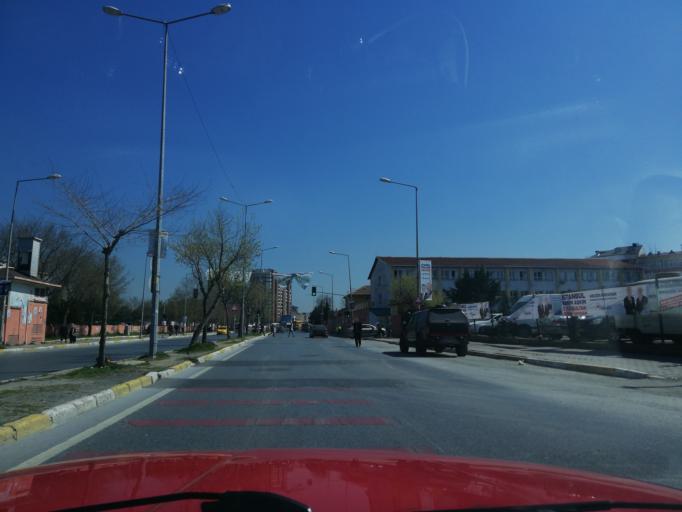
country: TR
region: Istanbul
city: Sisli
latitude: 41.0800
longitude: 28.9329
